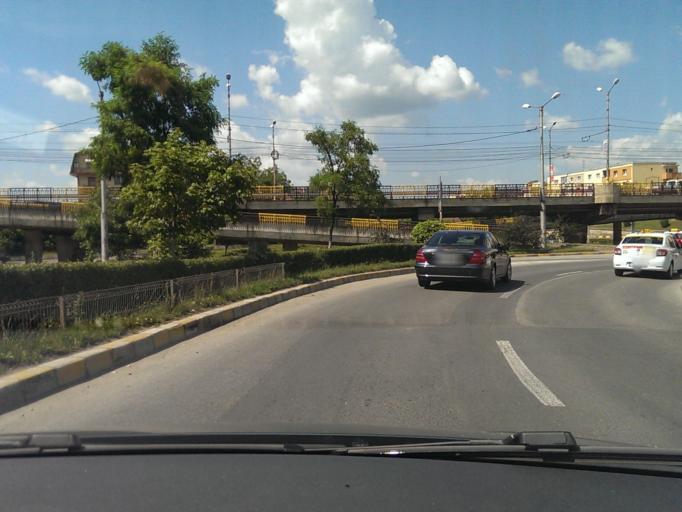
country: RO
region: Cluj
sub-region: Municipiul Cluj-Napoca
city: Cluj-Napoca
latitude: 46.7786
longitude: 23.6198
